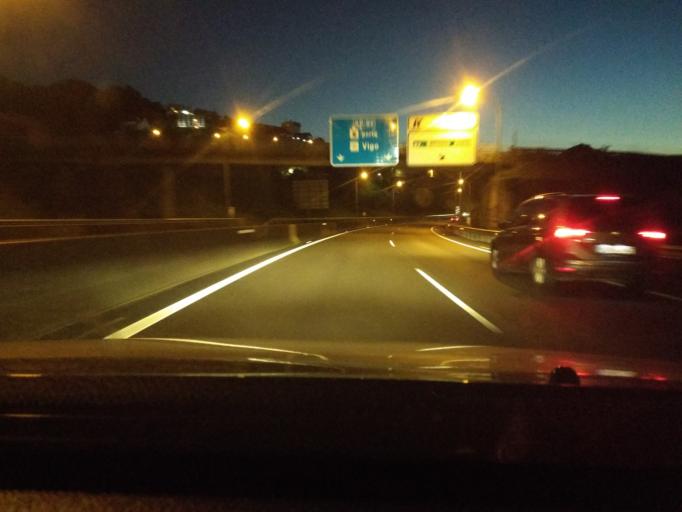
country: ES
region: Galicia
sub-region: Provincia de Pontevedra
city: Vigo
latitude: 42.2508
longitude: -8.6865
